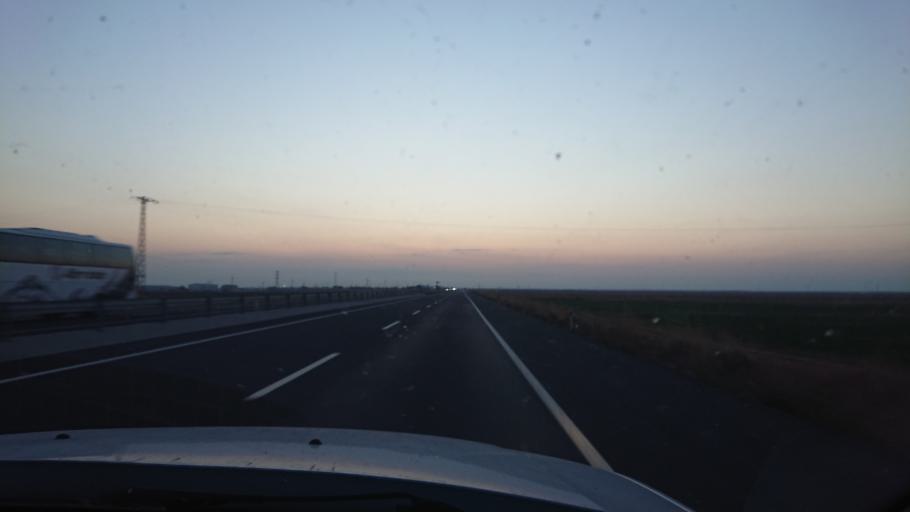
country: TR
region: Aksaray
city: Yesilova
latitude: 38.3067
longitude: 33.8173
